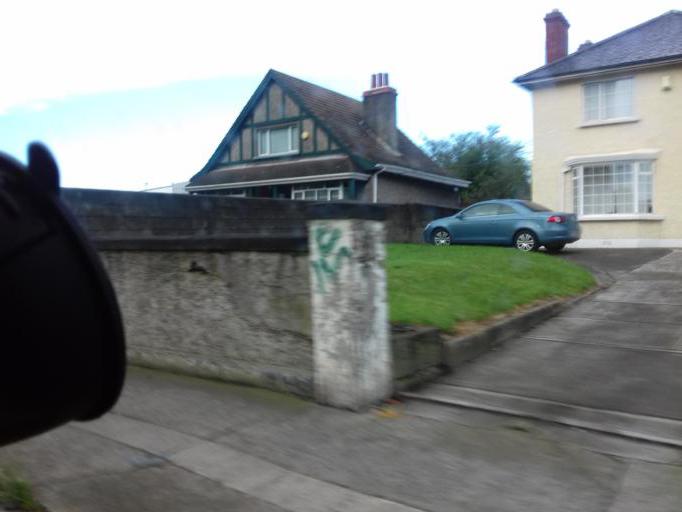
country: IE
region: Leinster
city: Cabra
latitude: 53.3585
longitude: -6.2877
